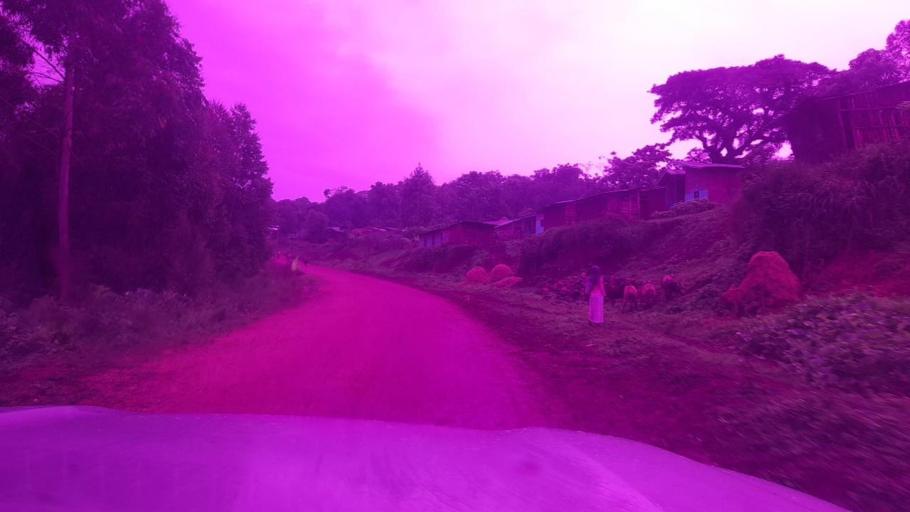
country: ET
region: Southern Nations, Nationalities, and People's Region
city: Bonga
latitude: 7.4413
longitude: 36.1672
